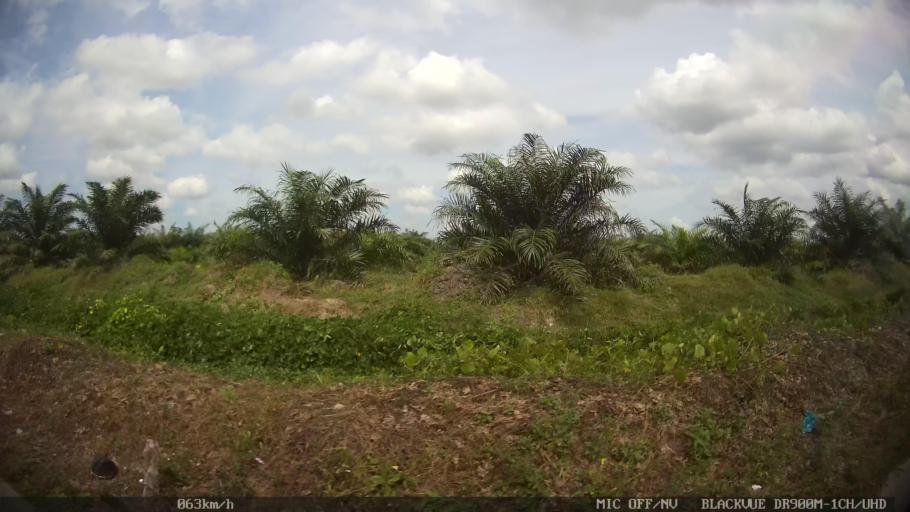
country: ID
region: North Sumatra
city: Percut
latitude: 3.5836
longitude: 98.8409
